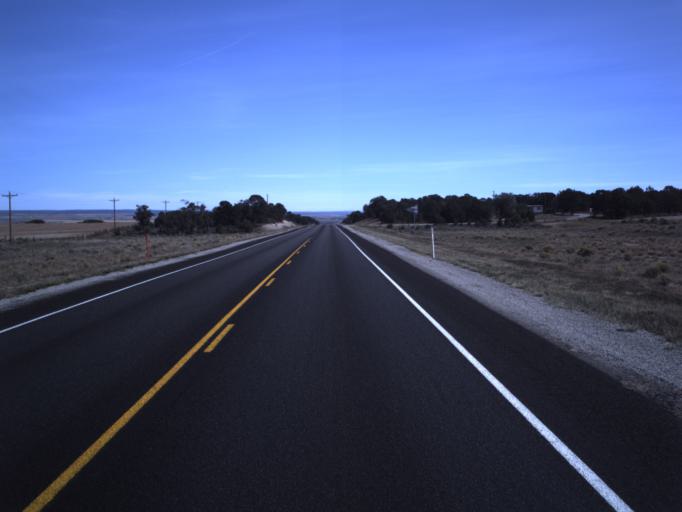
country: US
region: Colorado
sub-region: Dolores County
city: Dove Creek
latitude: 37.8275
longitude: -109.0804
